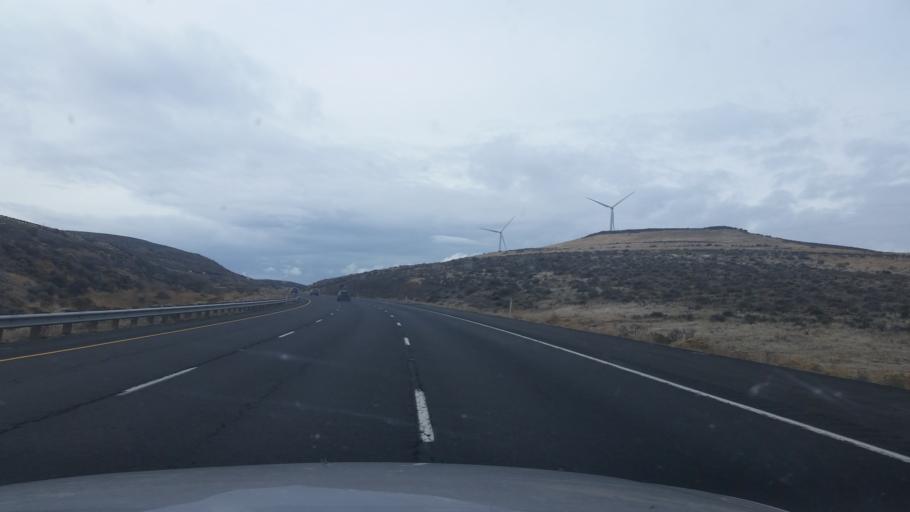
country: US
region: Washington
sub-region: Kittitas County
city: Kittitas
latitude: 46.9450
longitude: -120.1620
